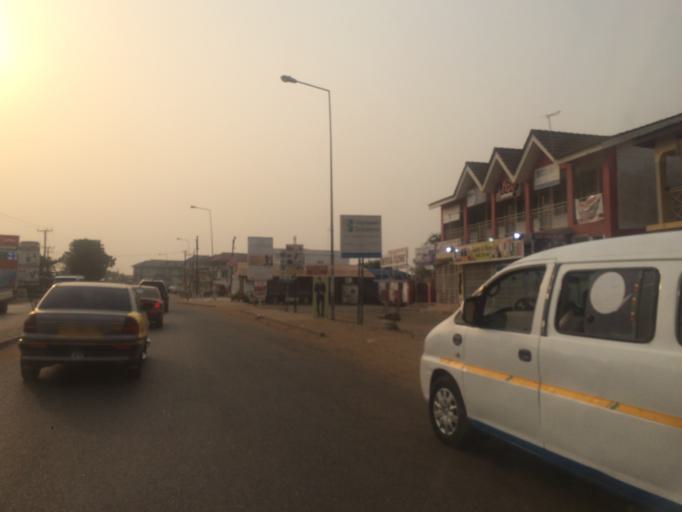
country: GH
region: Greater Accra
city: Nungua
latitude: 5.6376
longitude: -0.1047
